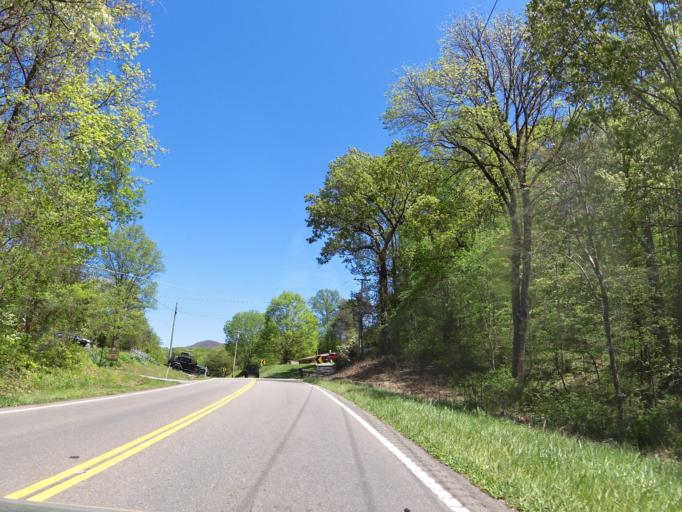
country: US
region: Tennessee
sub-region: Unicoi County
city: Banner Hill
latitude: 36.1748
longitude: -82.5218
